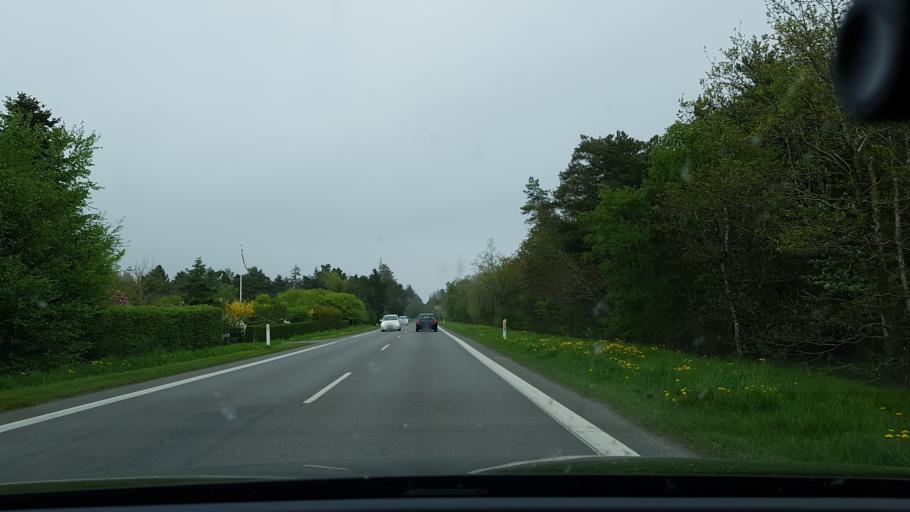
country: DK
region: Capital Region
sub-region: Bornholm Kommune
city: Nexo
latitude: 55.0463
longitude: 15.1108
